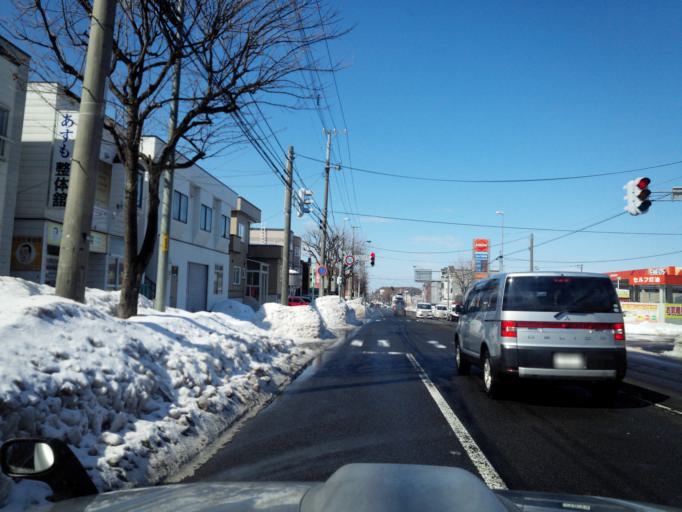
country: JP
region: Hokkaido
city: Kitahiroshima
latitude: 42.9997
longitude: 141.4496
